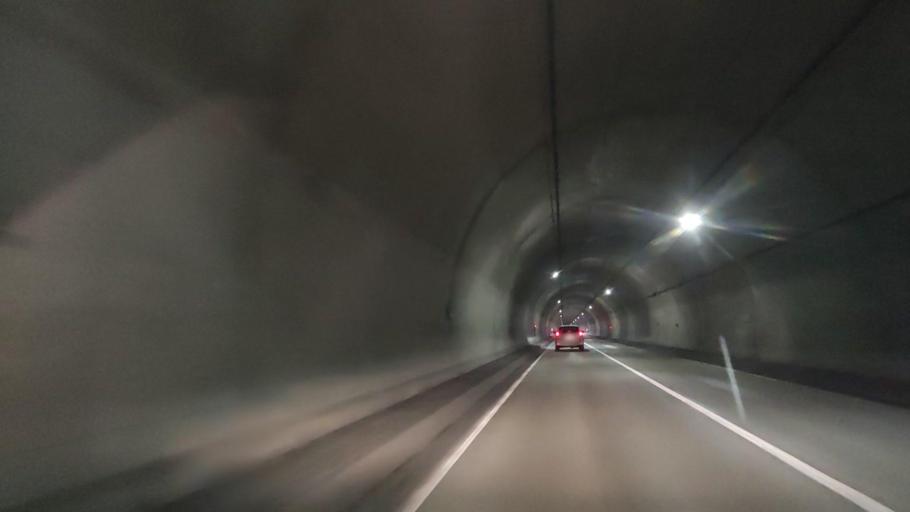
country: JP
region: Hokkaido
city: Ishikari
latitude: 43.5334
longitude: 141.3933
